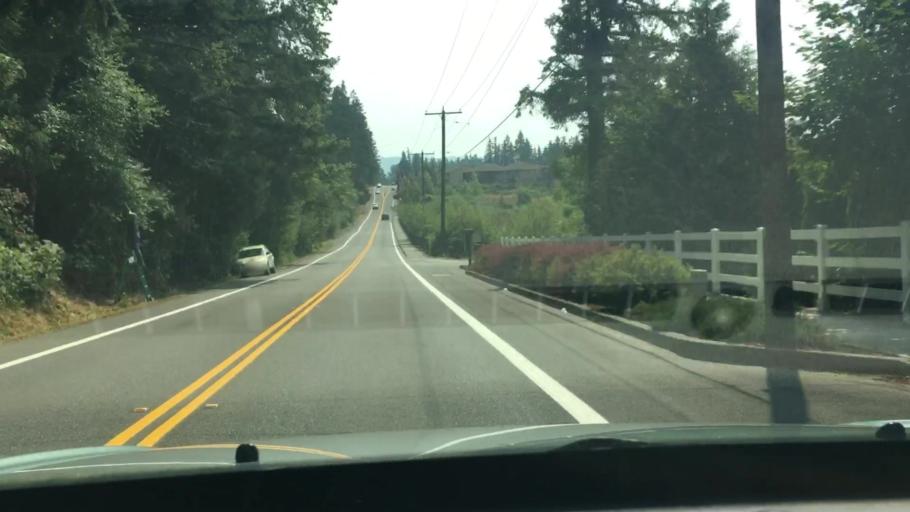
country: US
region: Washington
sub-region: King County
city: City of Sammamish
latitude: 47.5978
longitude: -122.0571
